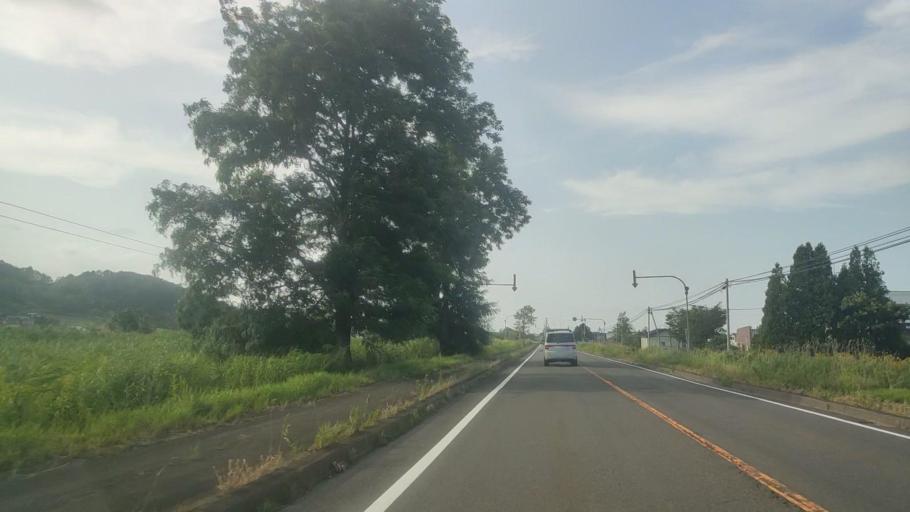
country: JP
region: Hokkaido
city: Iwamizawa
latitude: 43.0004
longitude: 141.7889
